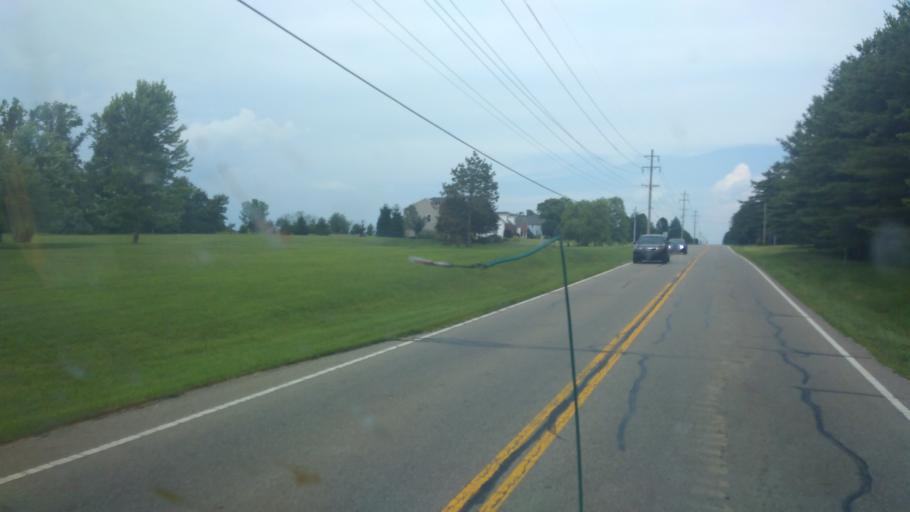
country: US
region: Ohio
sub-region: Fairfield County
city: Lancaster
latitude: 39.7681
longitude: -82.5876
